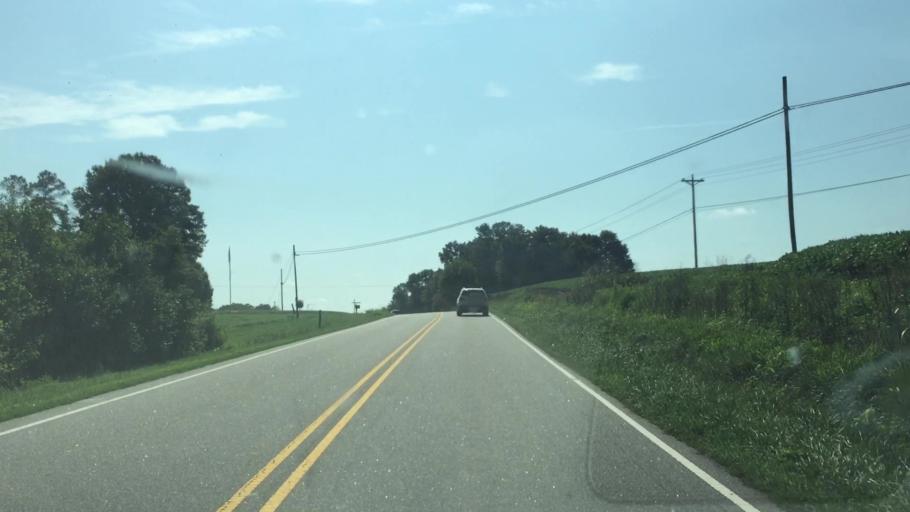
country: US
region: North Carolina
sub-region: Union County
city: Unionville
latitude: 35.1344
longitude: -80.4560
